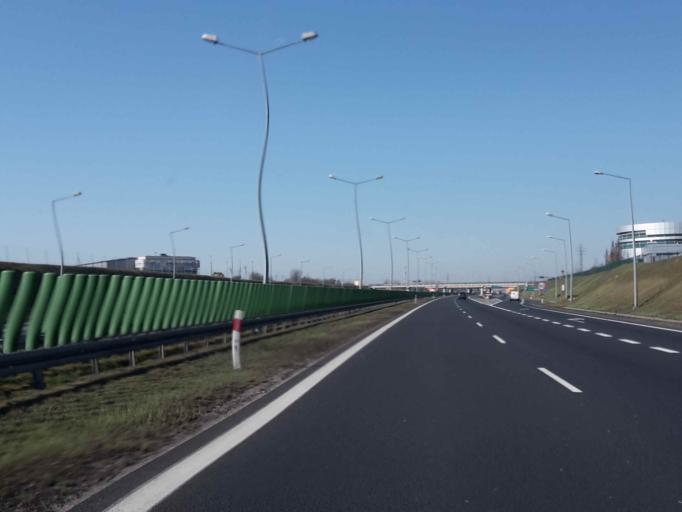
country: PL
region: Greater Poland Voivodeship
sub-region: Powiat poznanski
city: Komorniki
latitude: 52.3507
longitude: 16.8479
